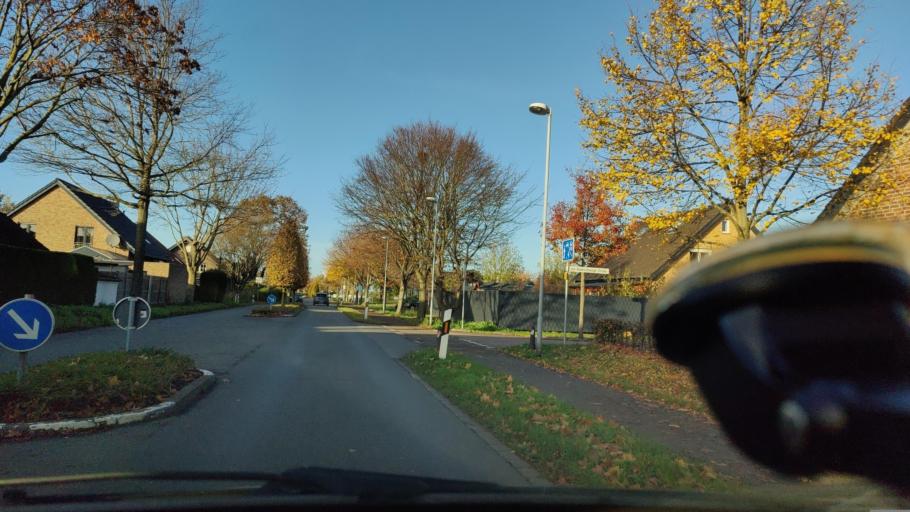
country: DE
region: North Rhine-Westphalia
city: Straelen
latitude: 51.4502
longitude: 6.2662
